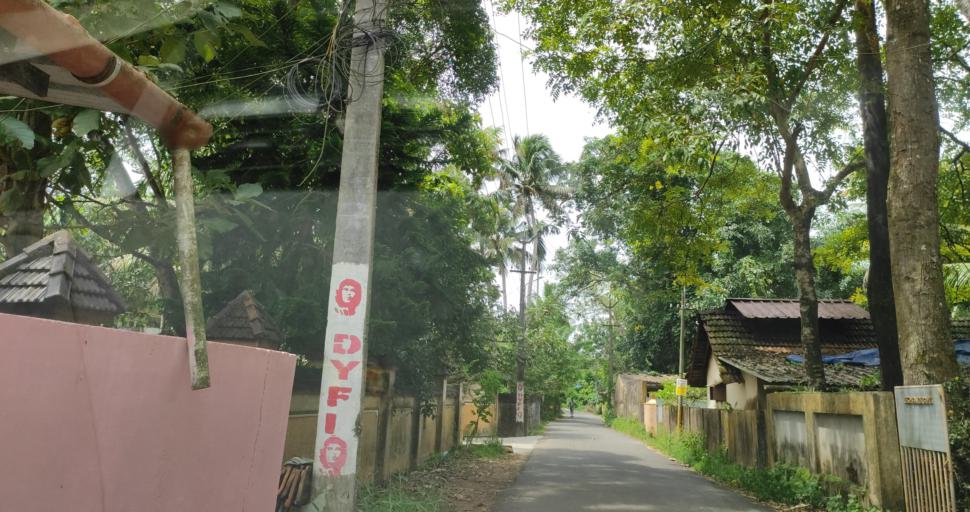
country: IN
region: Kerala
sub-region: Alappuzha
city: Shertallai
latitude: 9.6772
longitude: 76.3579
